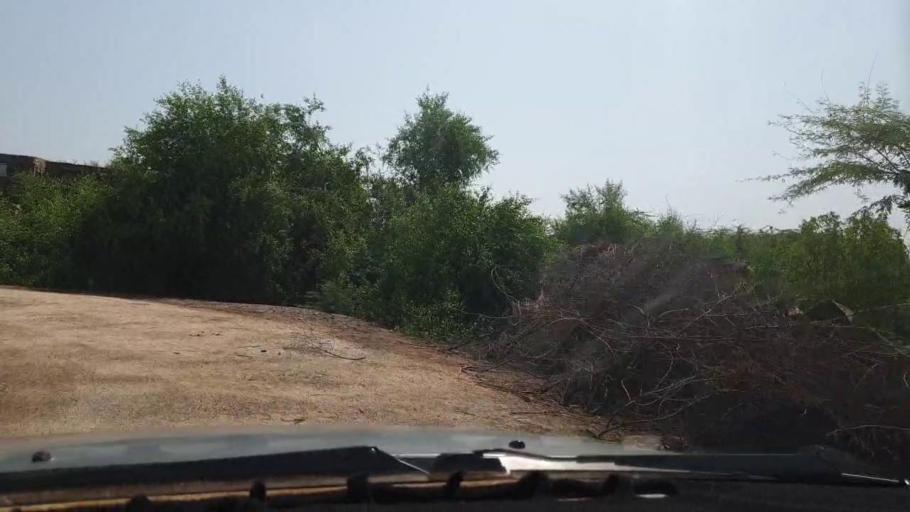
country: PK
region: Sindh
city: Tando Ghulam Ali
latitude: 25.1424
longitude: 68.7753
